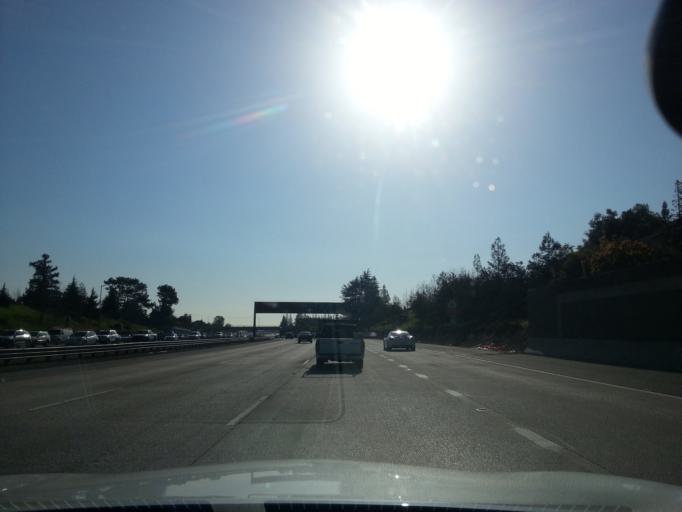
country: US
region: California
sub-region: Santa Clara County
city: Monte Sereno
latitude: 37.2603
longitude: -121.9705
